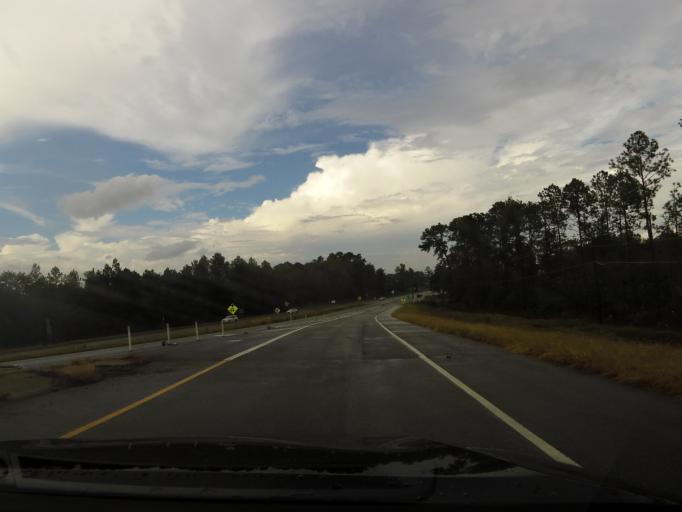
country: US
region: Georgia
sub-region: Wayne County
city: Jesup
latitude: 31.6244
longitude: -81.8671
